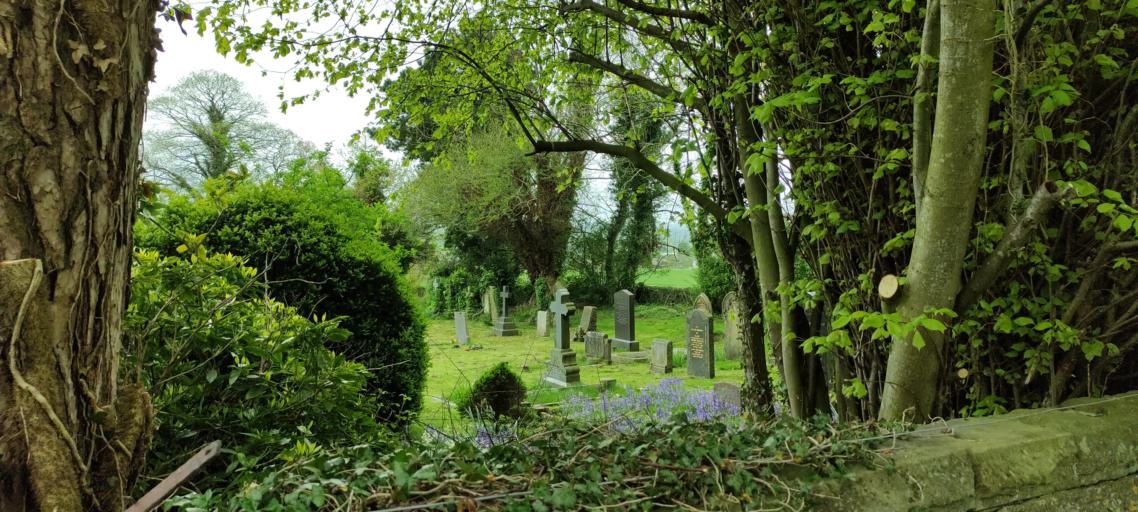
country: GB
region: England
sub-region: North Yorkshire
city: Ingleton
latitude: 54.1498
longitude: -2.4570
